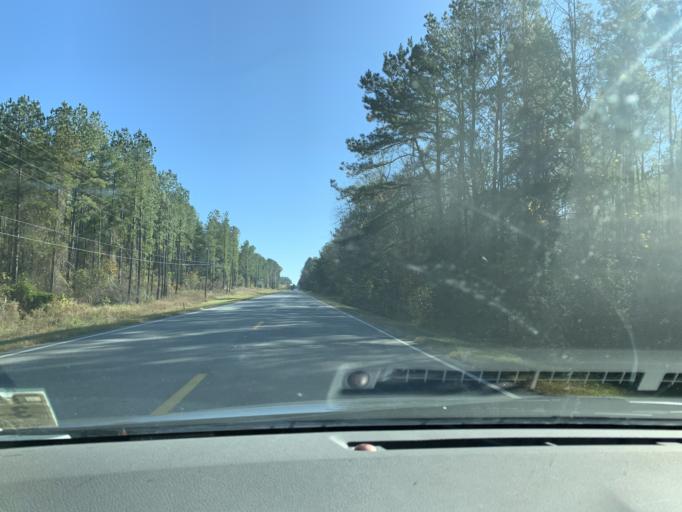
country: US
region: Georgia
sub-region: Ben Hill County
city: Fitzgerald
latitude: 31.7730
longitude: -83.0493
